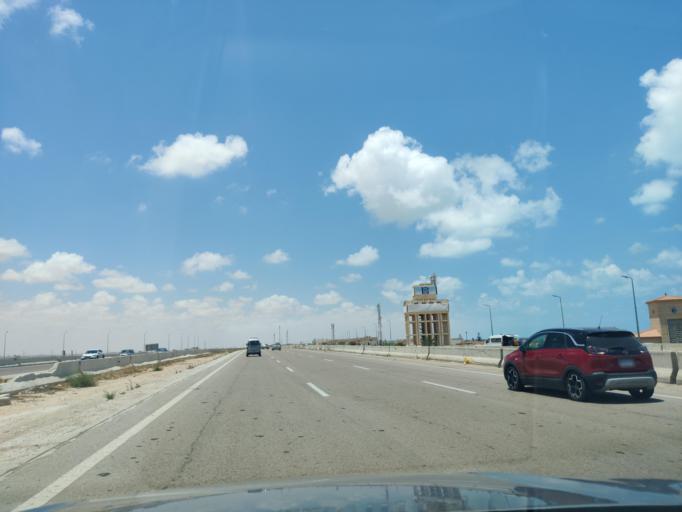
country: EG
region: Muhafazat Matruh
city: Al `Alamayn
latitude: 30.8130
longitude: 29.0569
